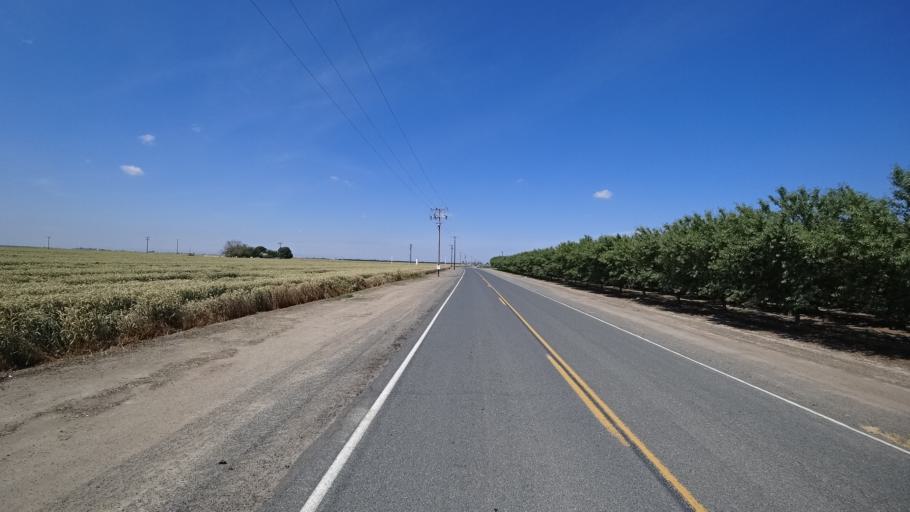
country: US
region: California
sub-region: Tulare County
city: Goshen
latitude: 36.2691
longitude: -119.5083
